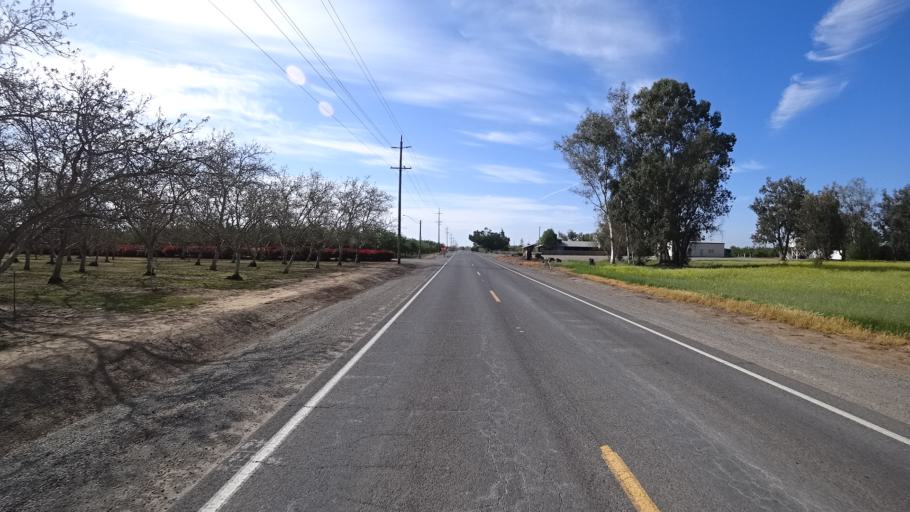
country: US
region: California
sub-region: Glenn County
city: Hamilton City
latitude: 39.6436
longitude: -122.0075
